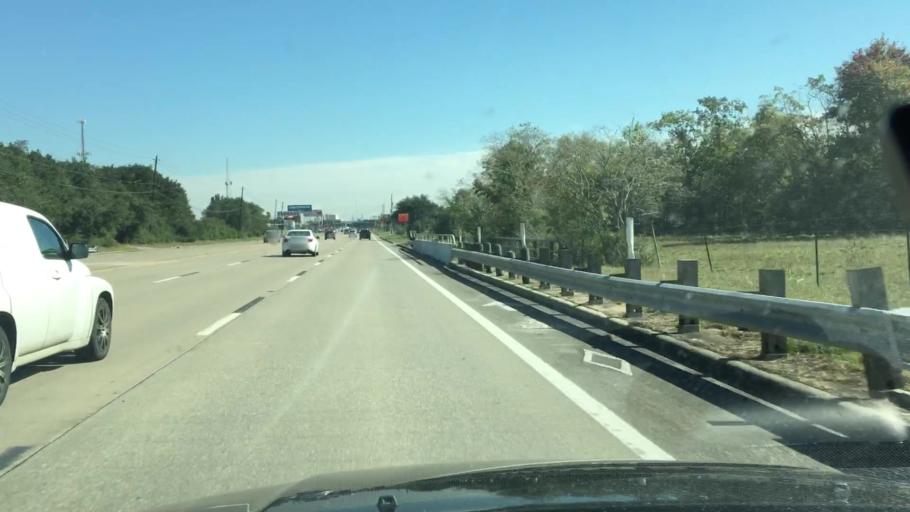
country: US
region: Texas
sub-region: Harris County
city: Webster
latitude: 29.5239
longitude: -95.1459
